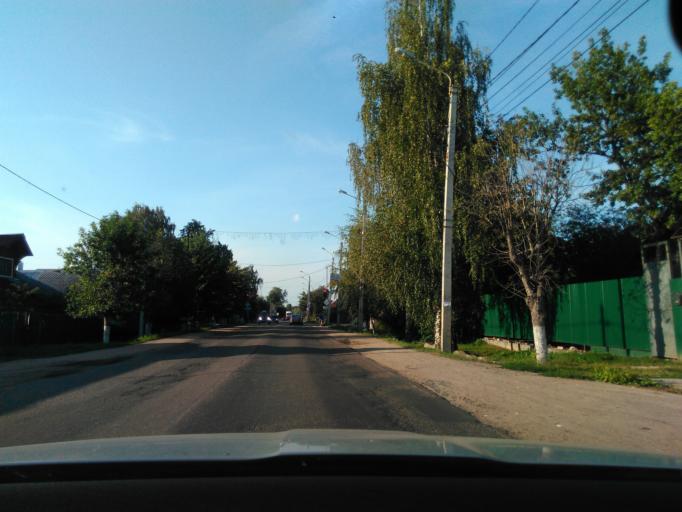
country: RU
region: Tverskaya
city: Konakovo
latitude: 56.7011
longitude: 36.7678
